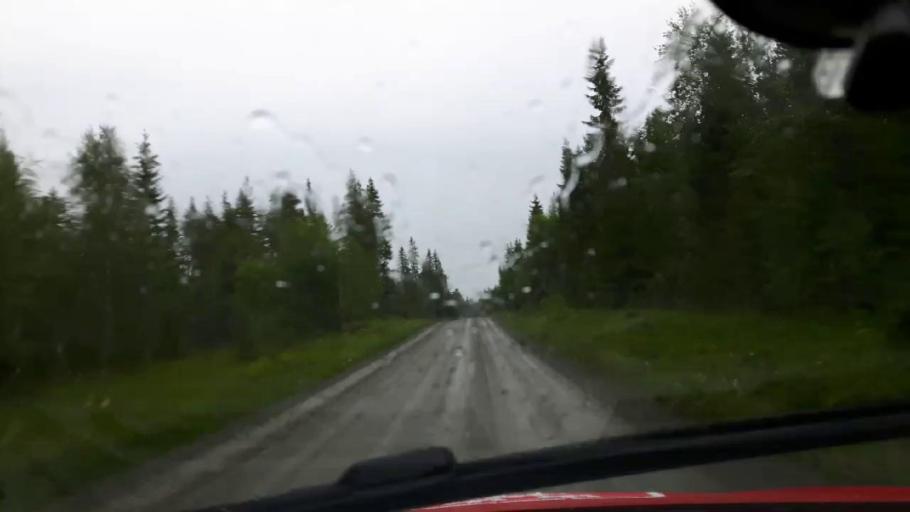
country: SE
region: Jaemtland
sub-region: OEstersunds Kommun
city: Brunflo
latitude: 62.9739
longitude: 14.8338
